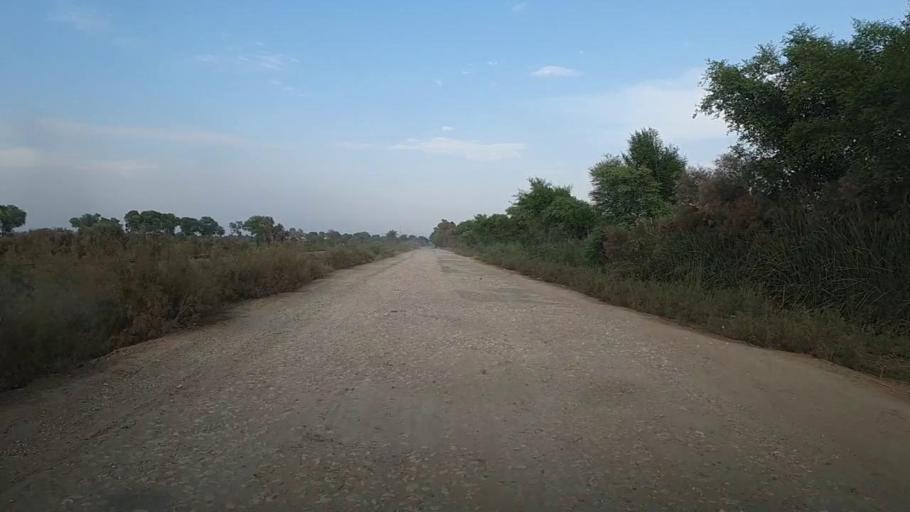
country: PK
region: Sindh
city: Thul
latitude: 28.2901
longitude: 68.8716
